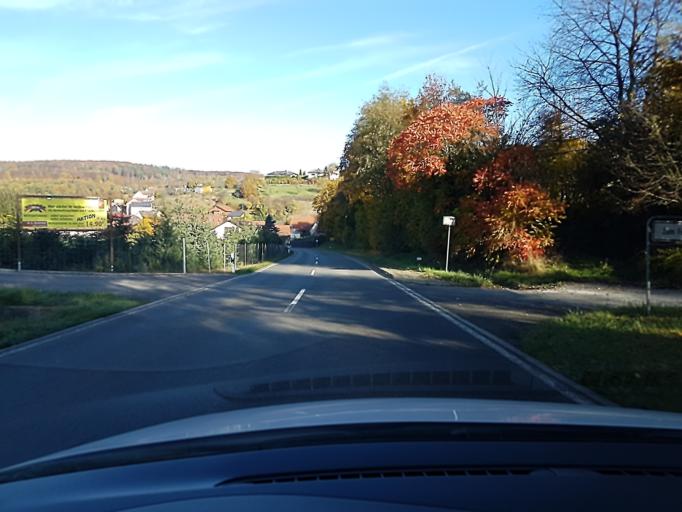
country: DE
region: Baden-Wuerttemberg
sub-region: Karlsruhe Region
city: Mosbach
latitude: 49.3824
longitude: 9.1946
